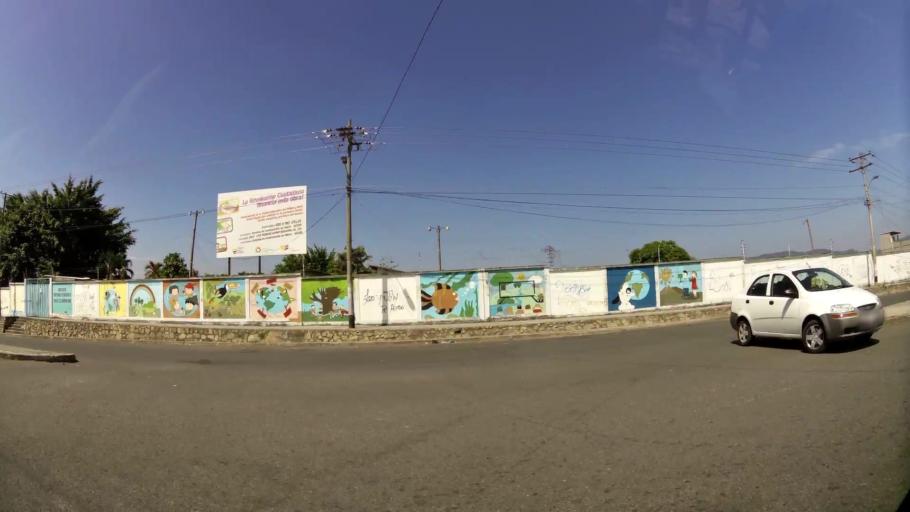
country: EC
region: Guayas
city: Eloy Alfaro
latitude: -2.1261
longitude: -79.9174
